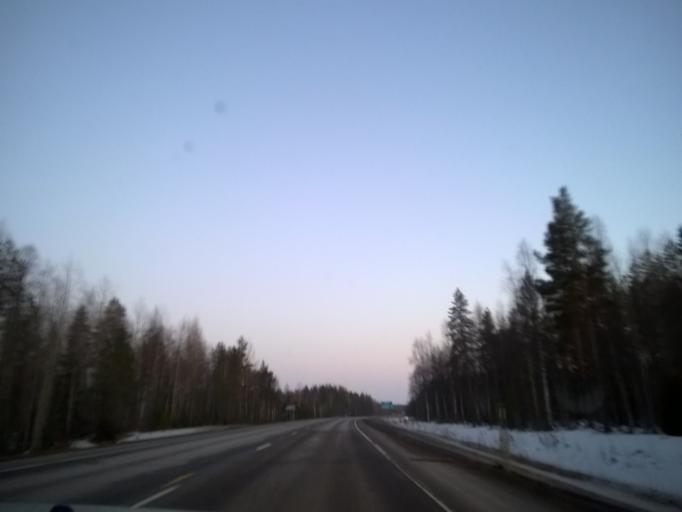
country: FI
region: Northern Ostrobothnia
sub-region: Nivala-Haapajaervi
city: Pyhaejaervi
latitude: 63.8068
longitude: 25.9128
